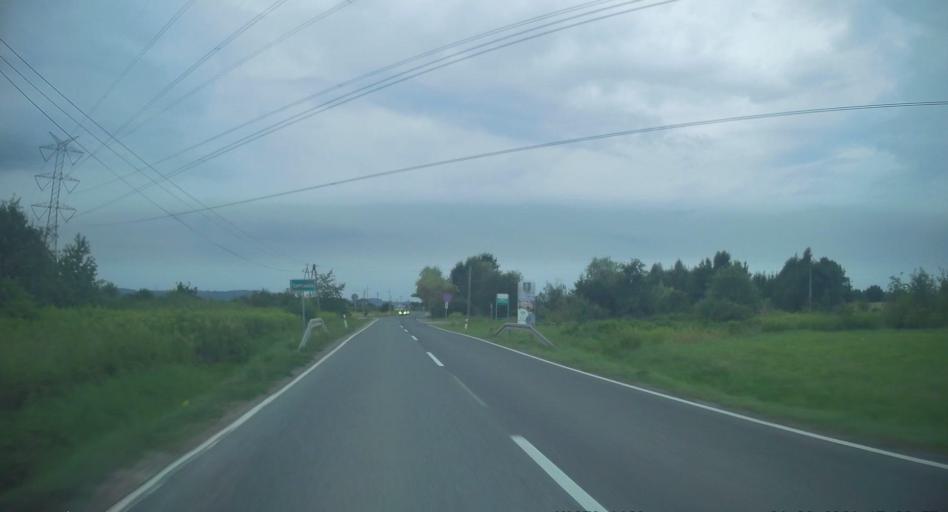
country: PL
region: Lesser Poland Voivodeship
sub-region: Powiat tarnowski
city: Wojnicz
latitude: 49.9851
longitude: 20.8400
